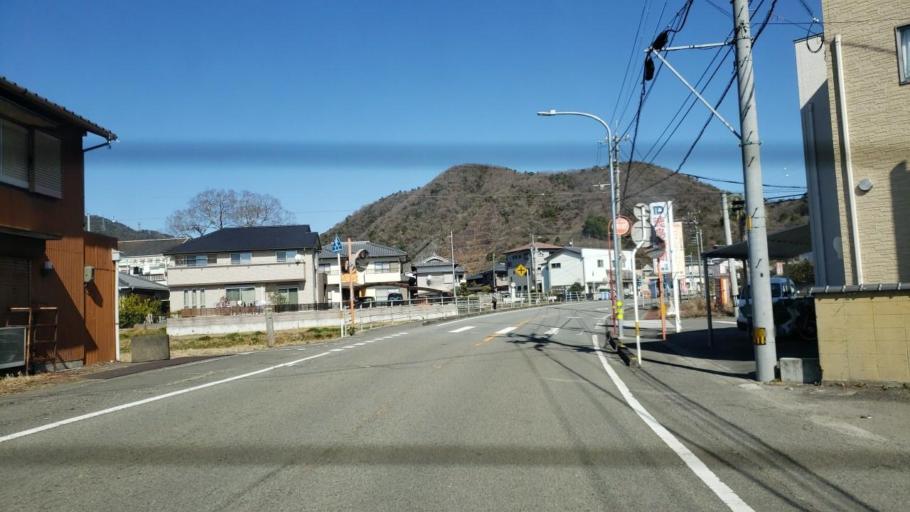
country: JP
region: Tokushima
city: Narutocho-mitsuishi
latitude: 34.1611
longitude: 134.5383
